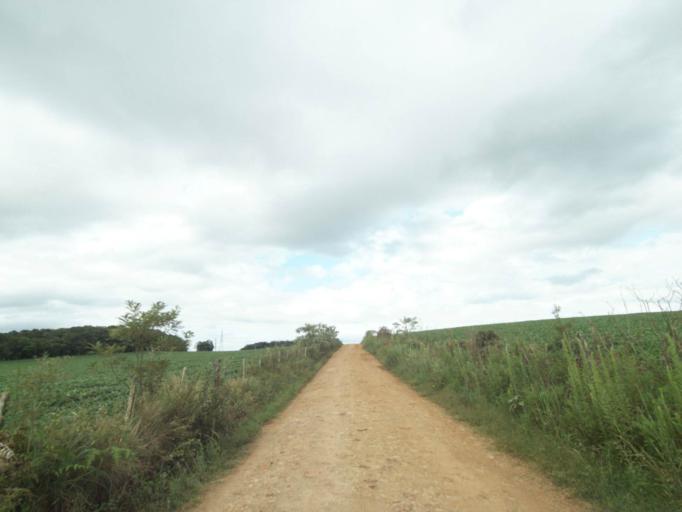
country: BR
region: Rio Grande do Sul
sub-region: Lagoa Vermelha
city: Lagoa Vermelha
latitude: -28.2008
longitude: -51.5143
